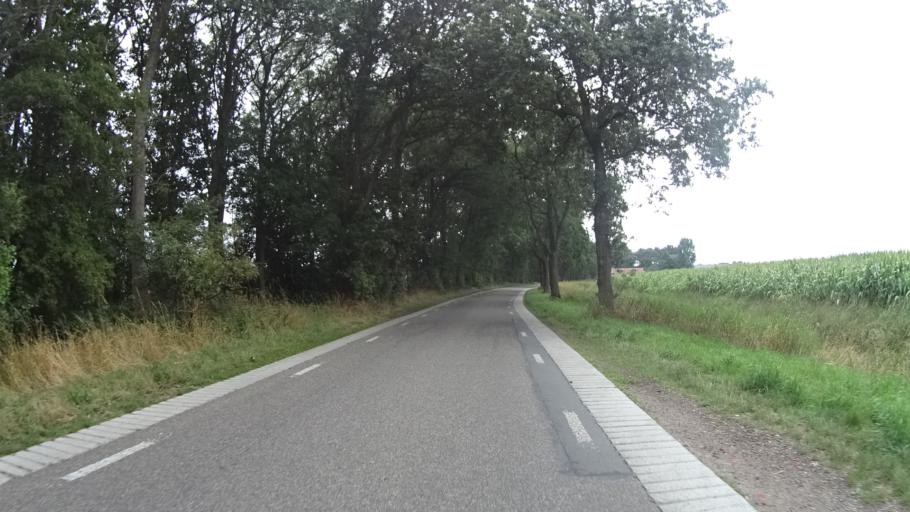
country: NL
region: Groningen
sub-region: Gemeente Slochteren
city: Slochteren
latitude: 53.1983
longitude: 6.8393
